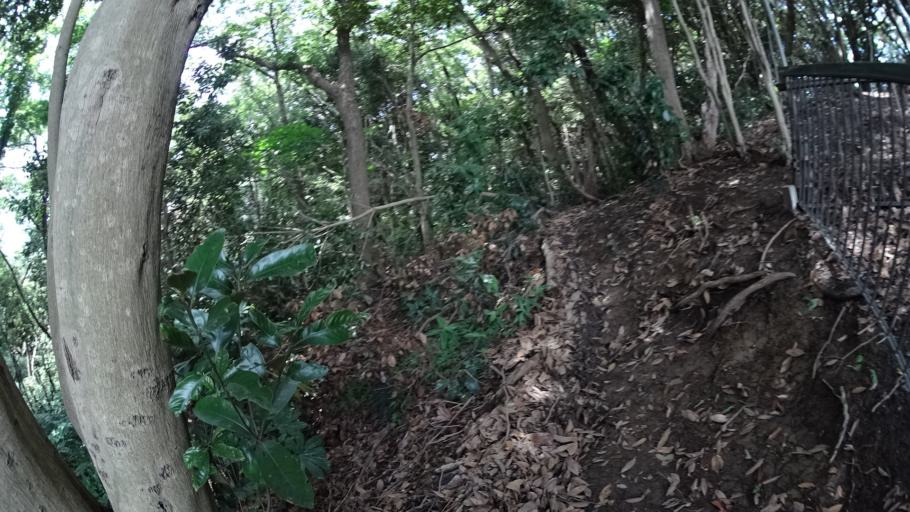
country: JP
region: Kanagawa
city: Yokosuka
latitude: 35.2096
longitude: 139.6702
